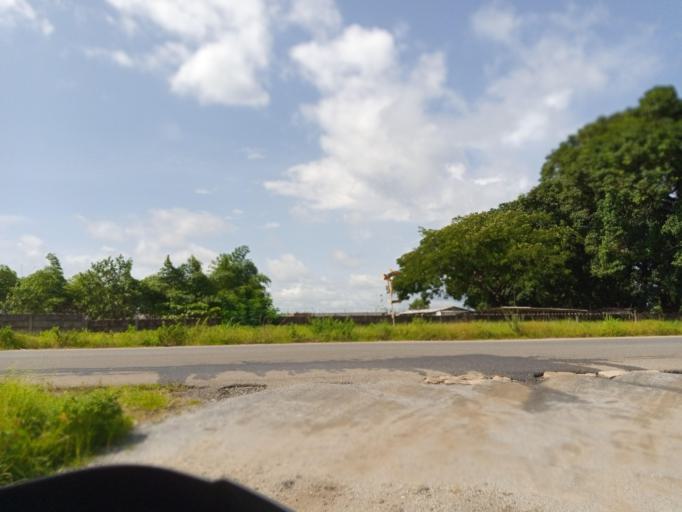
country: SL
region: Northern Province
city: Tintafor
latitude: 8.6164
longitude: -13.2071
